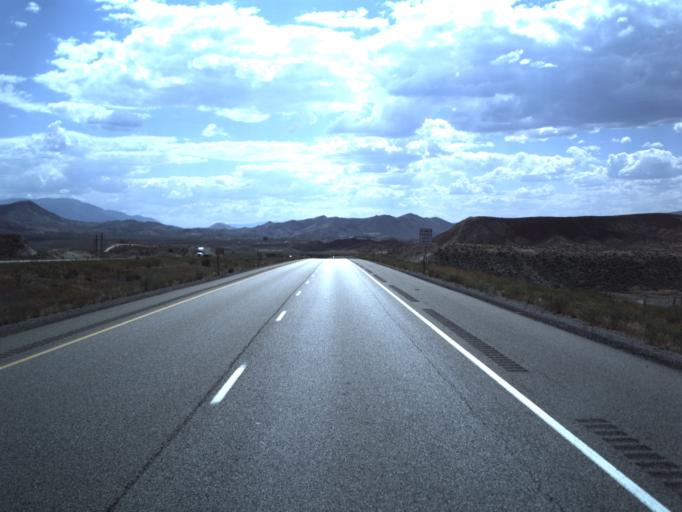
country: US
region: Utah
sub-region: Sevier County
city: Salina
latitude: 38.9255
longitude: -111.8728
